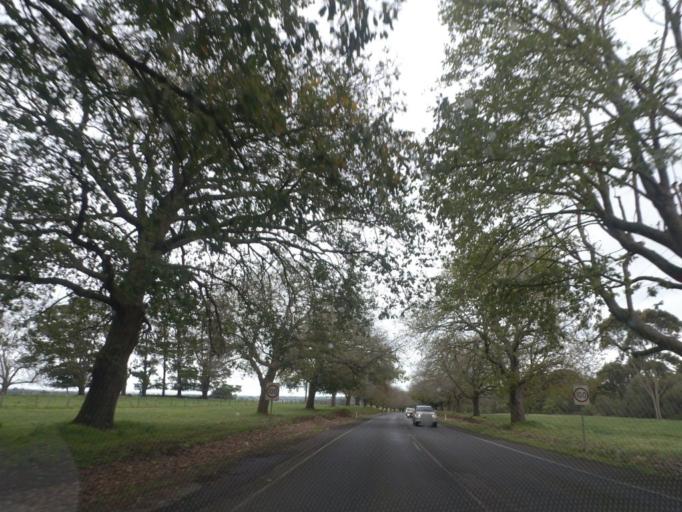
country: AU
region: Victoria
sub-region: Hume
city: Sunbury
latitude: -37.3417
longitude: 144.5293
